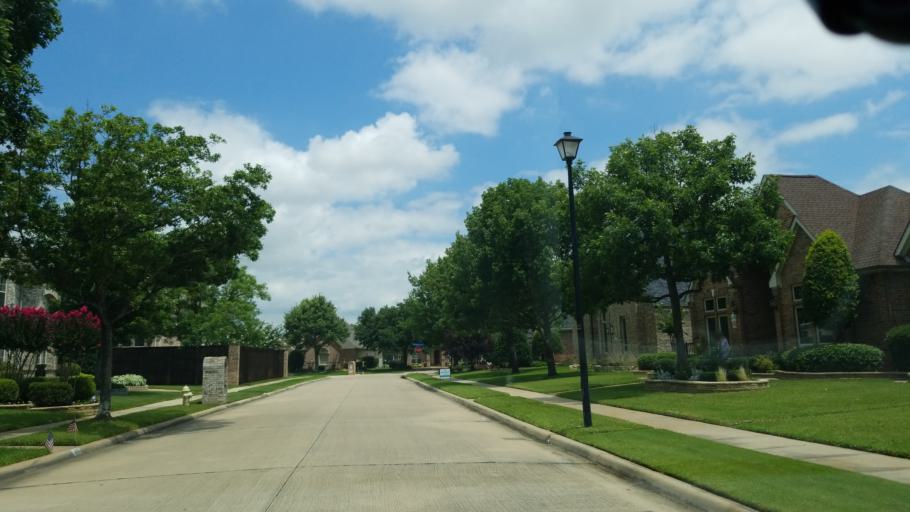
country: US
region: Texas
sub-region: Dallas County
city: Carrollton
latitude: 32.9593
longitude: -96.9518
